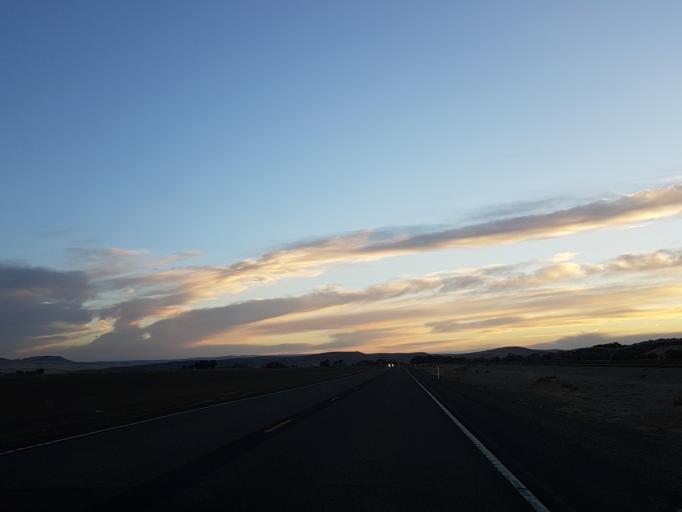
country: US
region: Oregon
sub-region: Malheur County
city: Vale
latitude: 43.9514
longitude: -117.2928
